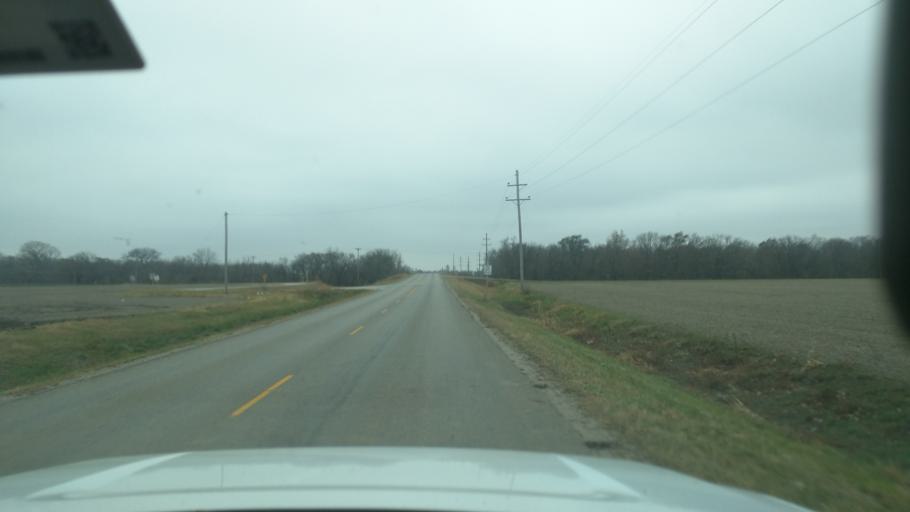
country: US
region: Kansas
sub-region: Lyon County
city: Emporia
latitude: 38.4744
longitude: -96.2530
